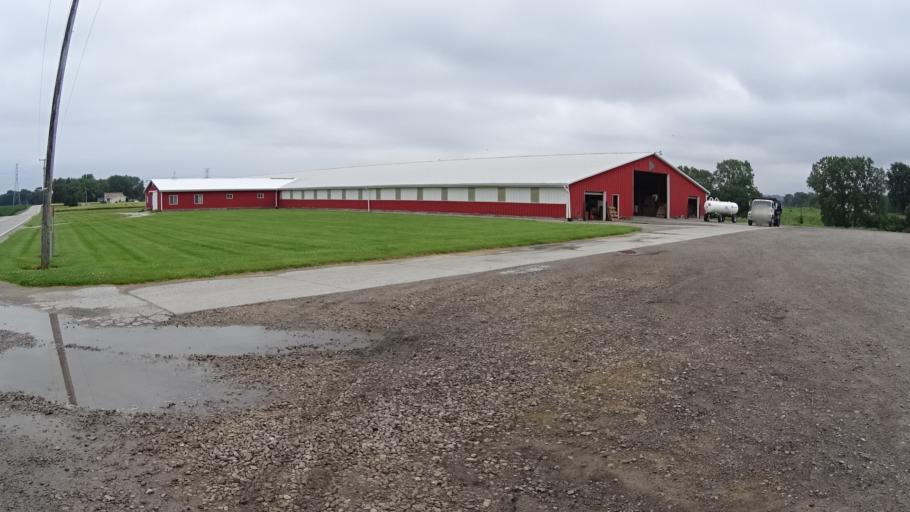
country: US
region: Ohio
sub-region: Erie County
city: Huron
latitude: 41.3299
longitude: -82.5382
